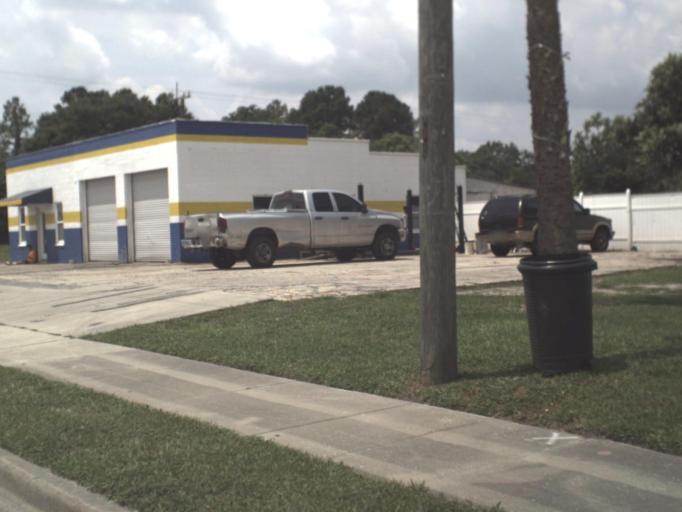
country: US
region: Florida
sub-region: Putnam County
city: Palatka
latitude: 29.6632
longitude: -81.6563
